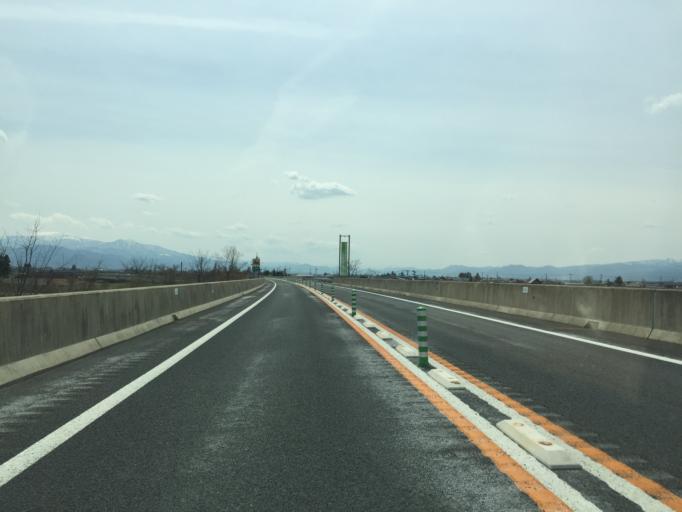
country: JP
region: Yamagata
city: Tendo
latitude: 38.3956
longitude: 140.3428
